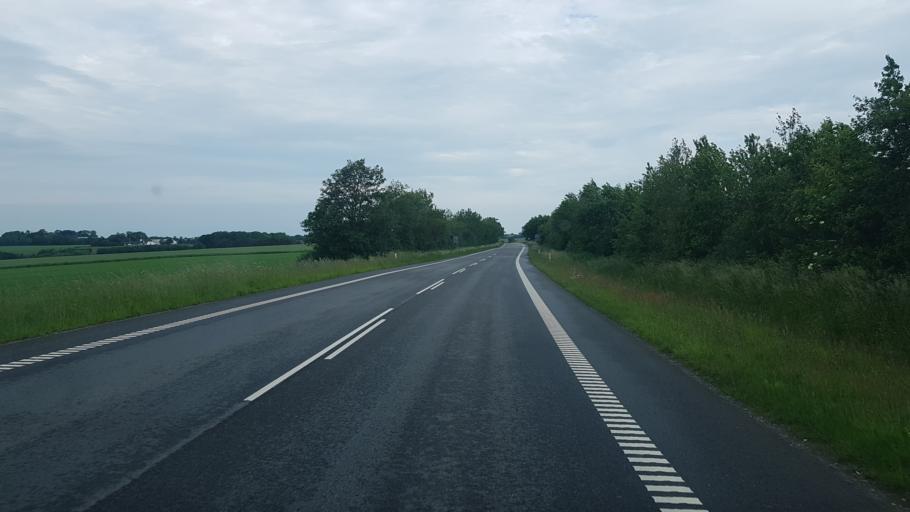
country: DK
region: South Denmark
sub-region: Vejen Kommune
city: Rodding
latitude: 55.3806
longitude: 9.0534
